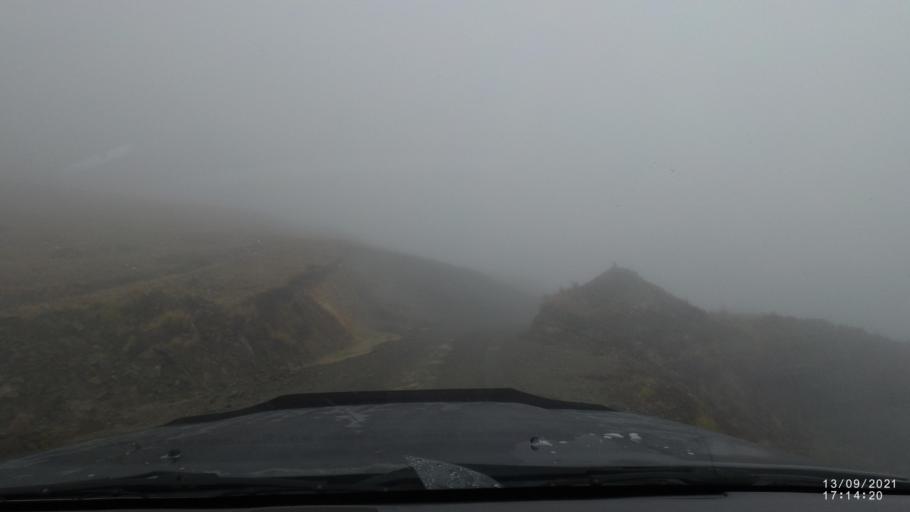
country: BO
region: Cochabamba
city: Colomi
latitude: -17.3426
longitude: -65.7523
